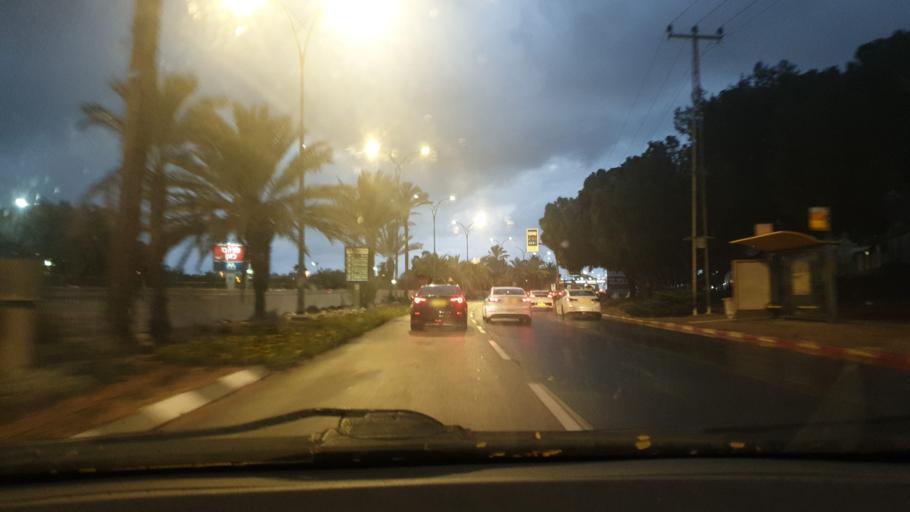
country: IL
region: Central District
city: Rishon LeZiyyon
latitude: 31.9776
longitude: 34.7887
